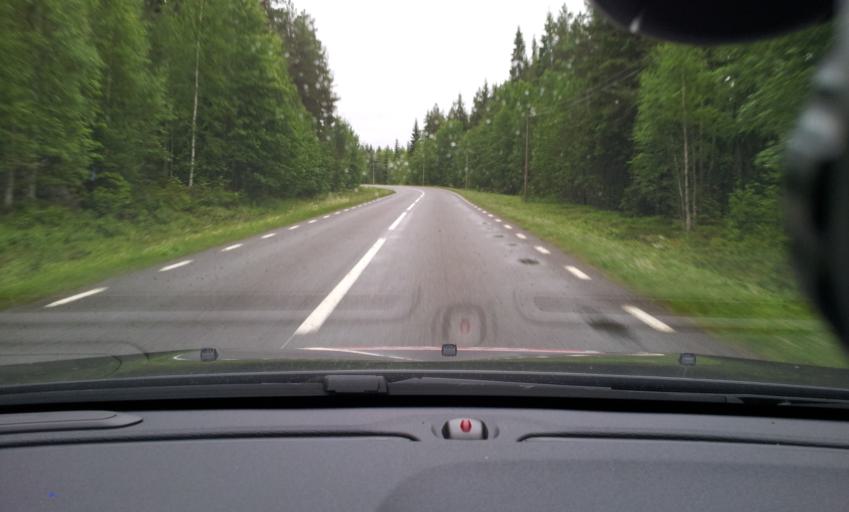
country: SE
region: Jaemtland
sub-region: Stroemsunds Kommun
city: Stroemsund
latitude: 63.4002
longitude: 15.6307
